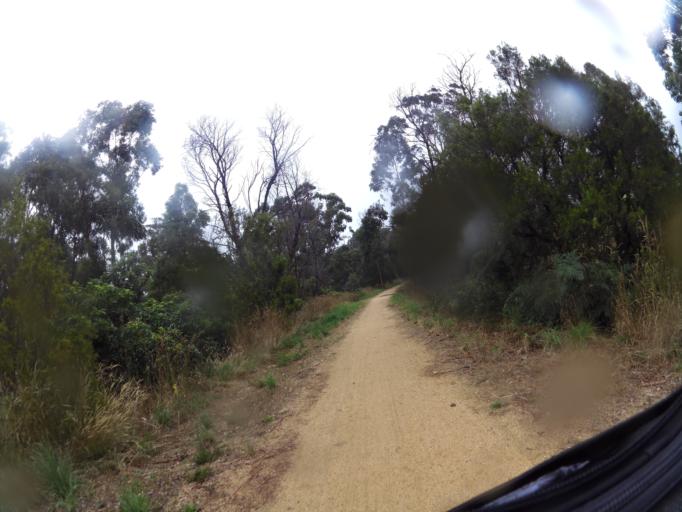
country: AU
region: Victoria
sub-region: East Gippsland
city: Lakes Entrance
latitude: -37.7650
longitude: 147.8210
